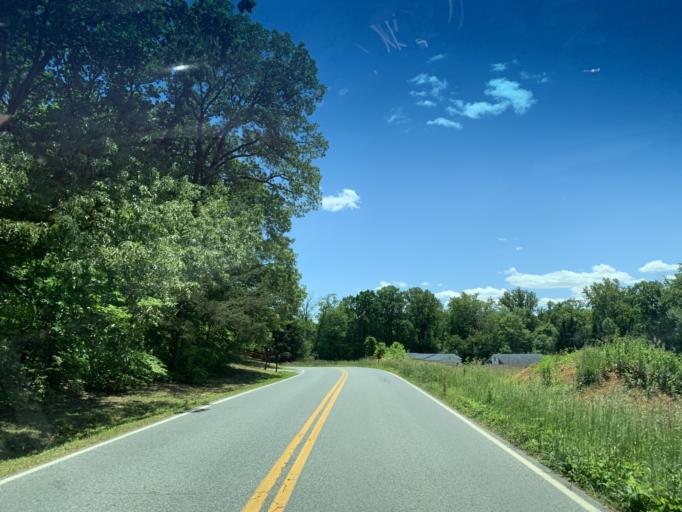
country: US
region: Maryland
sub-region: Cecil County
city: Charlestown
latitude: 39.6361
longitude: -76.0087
